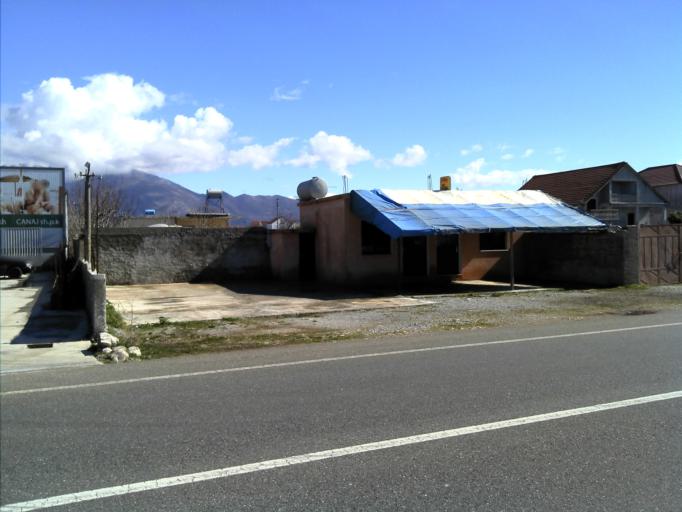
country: AL
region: Shkoder
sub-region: Rrethi i Malesia e Madhe
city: Grude-Fushe
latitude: 42.1570
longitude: 19.4730
